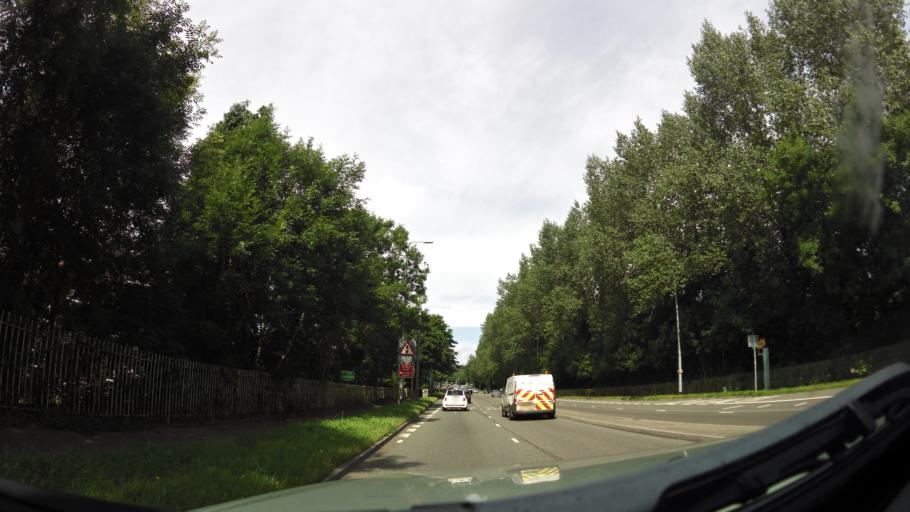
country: GB
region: Wales
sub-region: Cardiff
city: Radyr
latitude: 51.5217
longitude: -3.2260
